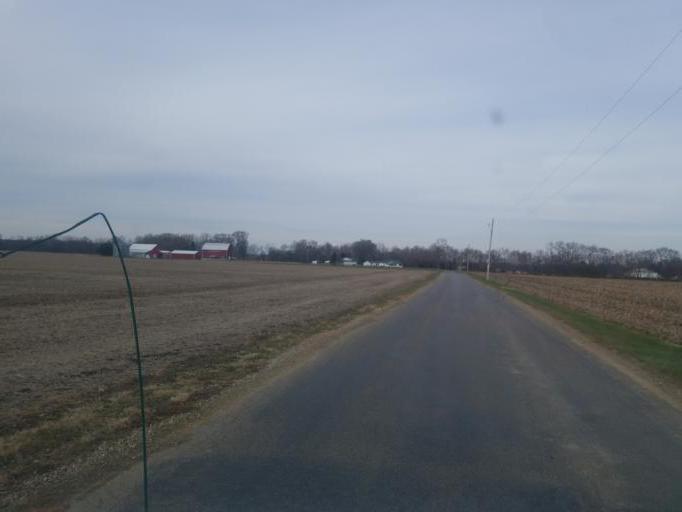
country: US
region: Ohio
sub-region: Knox County
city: Mount Vernon
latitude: 40.4199
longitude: -82.5339
